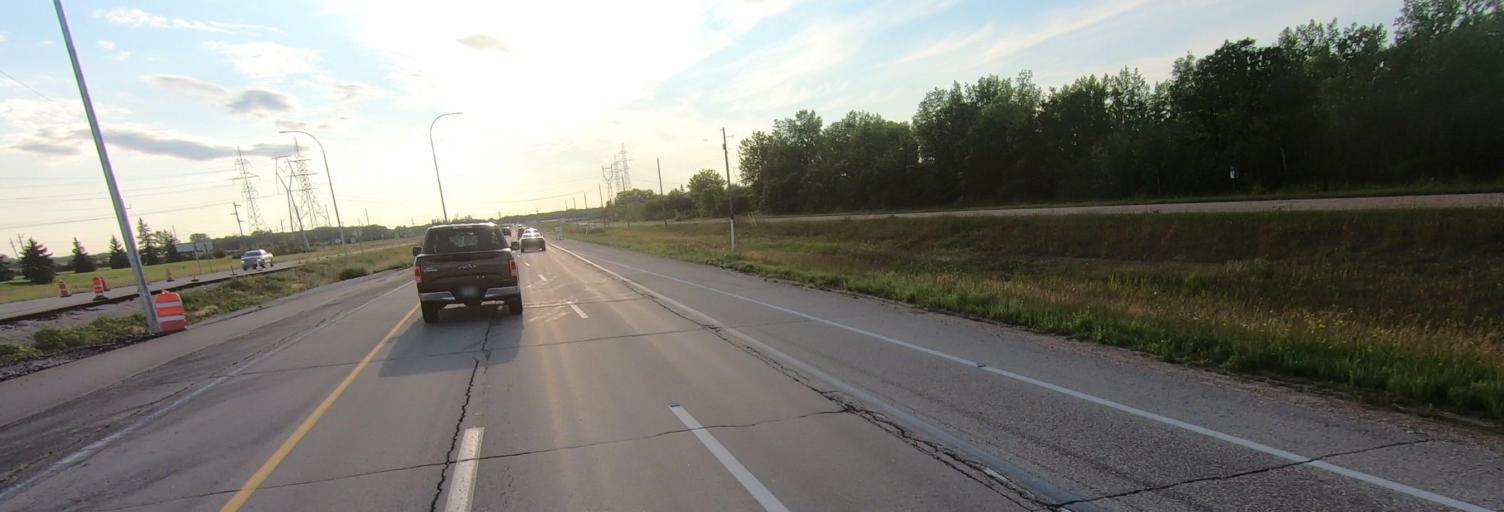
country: CA
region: Manitoba
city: Winnipeg
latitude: 49.9671
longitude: -96.9970
